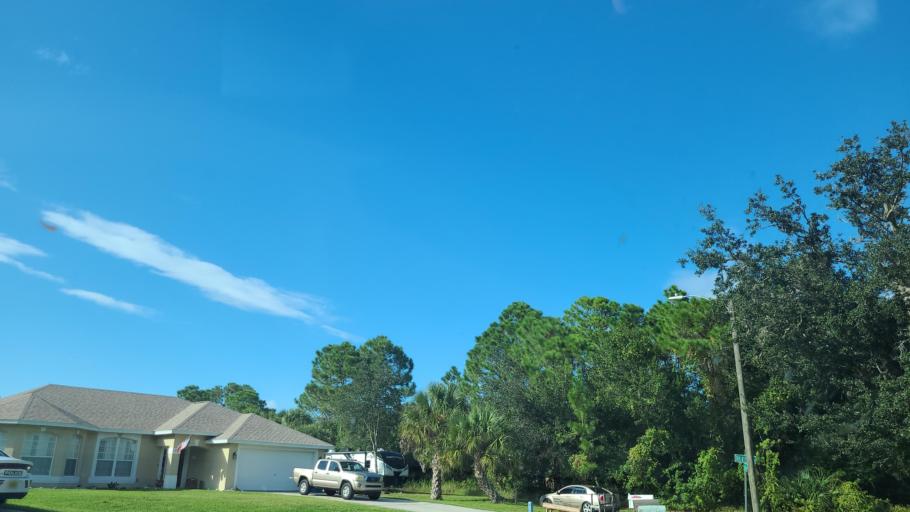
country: US
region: Florida
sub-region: Brevard County
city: June Park
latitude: 27.9835
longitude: -80.6710
